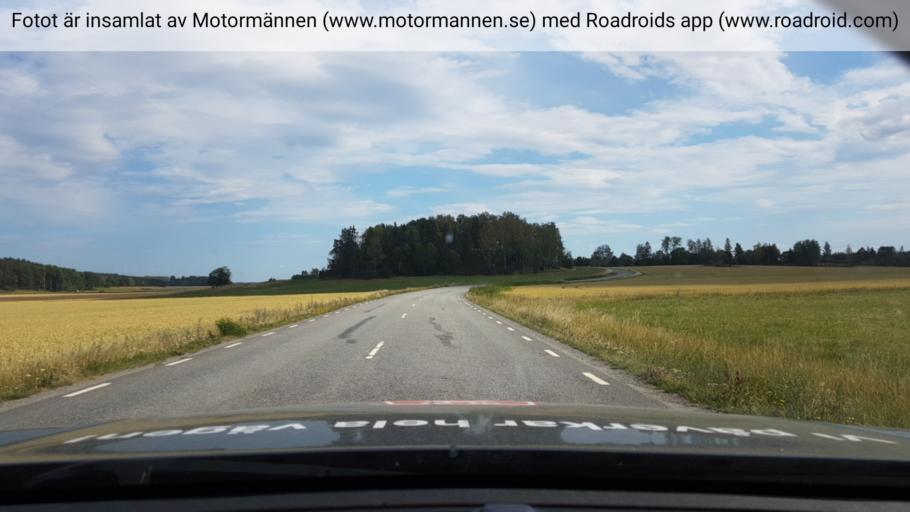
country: SE
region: Uppsala
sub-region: Enkopings Kommun
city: Grillby
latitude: 59.6503
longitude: 17.2615
